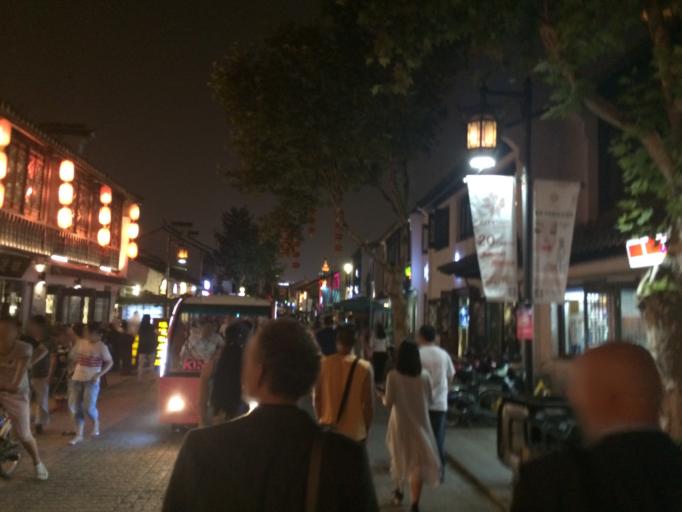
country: CN
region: Jiangsu Sheng
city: Nanchansi
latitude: 31.5609
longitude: 120.3097
